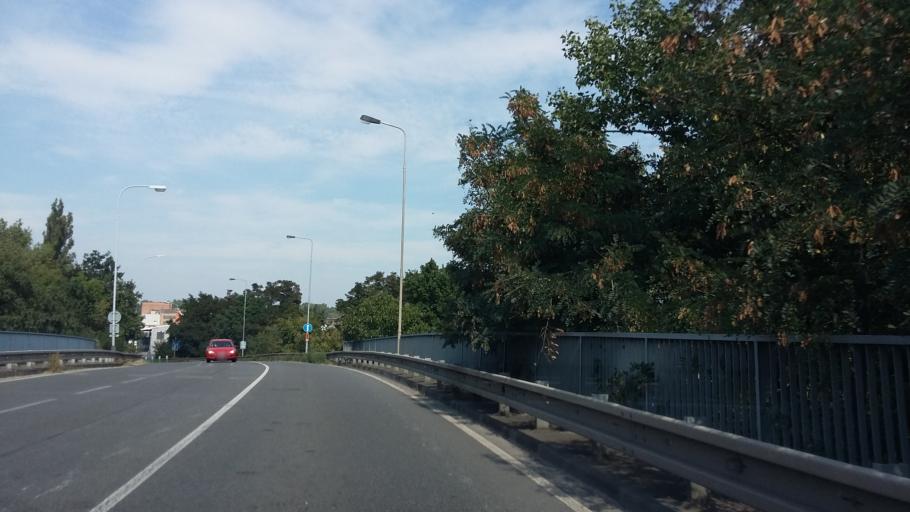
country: CZ
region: Central Bohemia
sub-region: Okres Kolin
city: Kolin
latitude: 50.0368
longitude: 15.2105
